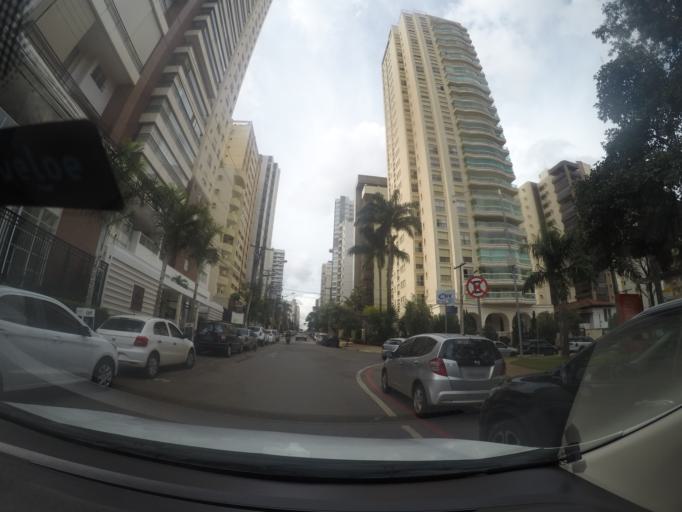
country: BR
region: Goias
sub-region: Goiania
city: Goiania
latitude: -16.7110
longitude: -49.2694
